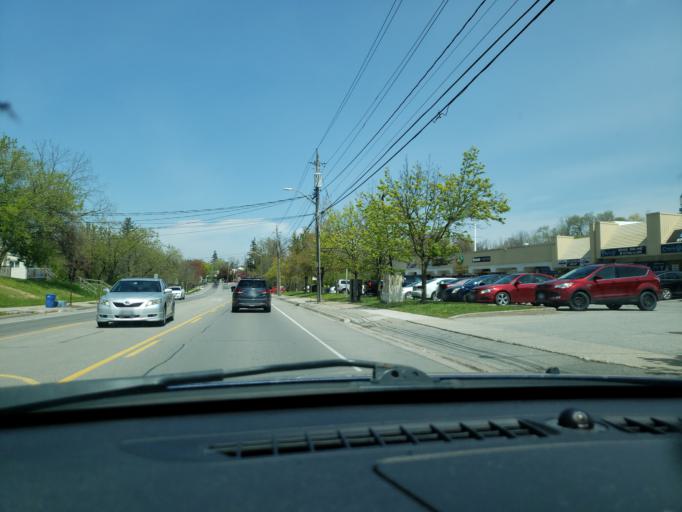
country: CA
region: Ontario
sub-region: Regional Municipality of Niagara
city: St. Catharines
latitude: 43.1561
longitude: -79.2144
